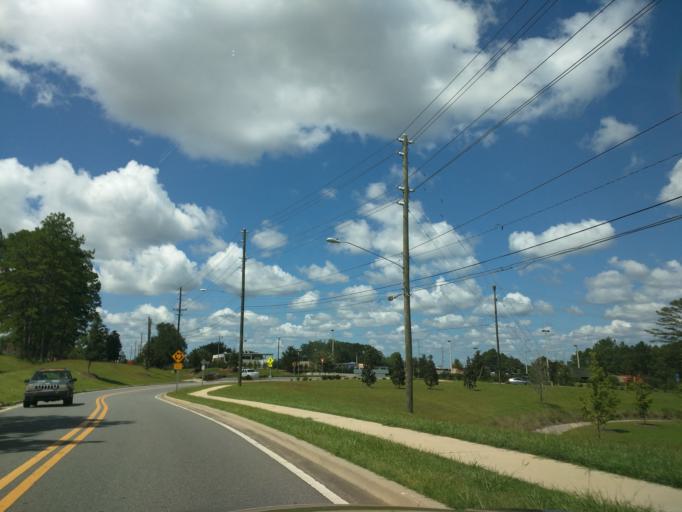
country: US
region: Florida
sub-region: Leon County
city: Tallahassee
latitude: 30.4510
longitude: -84.2230
